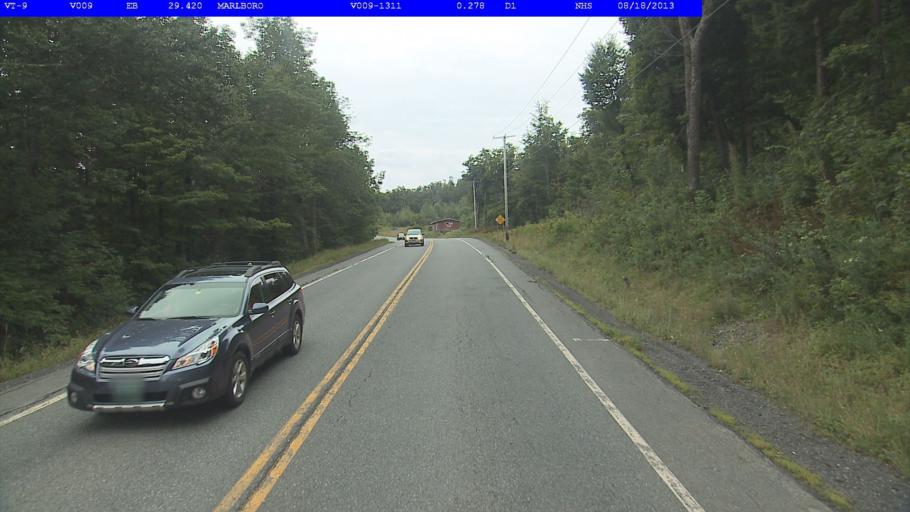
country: US
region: Vermont
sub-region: Windham County
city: Dover
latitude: 42.8561
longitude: -72.7990
